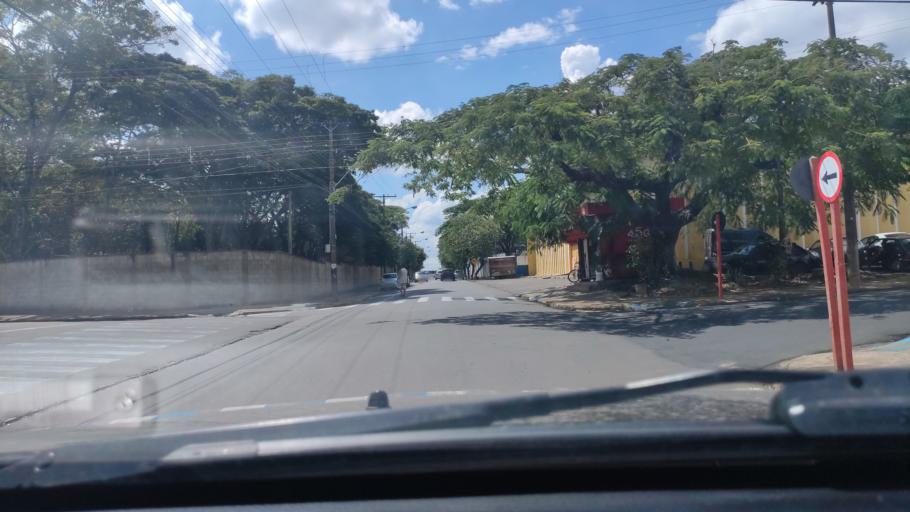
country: BR
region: Sao Paulo
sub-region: Sao Carlos
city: Sao Carlos
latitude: -22.0020
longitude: -47.8799
